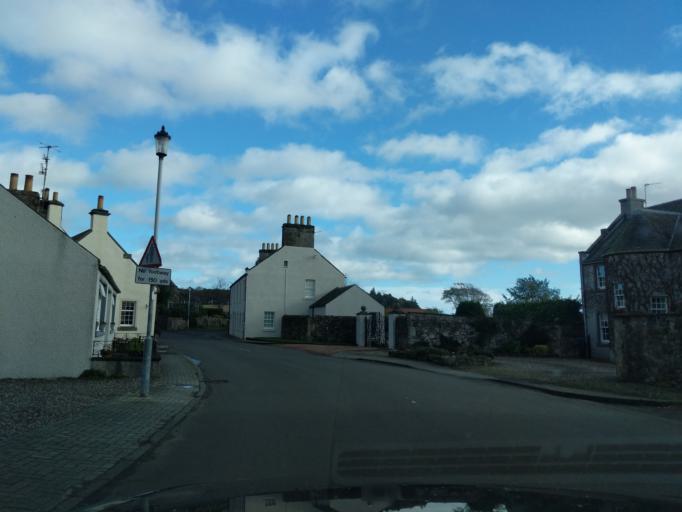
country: GB
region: Scotland
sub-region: Fife
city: Saint Monance
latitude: 56.2085
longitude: -2.8275
